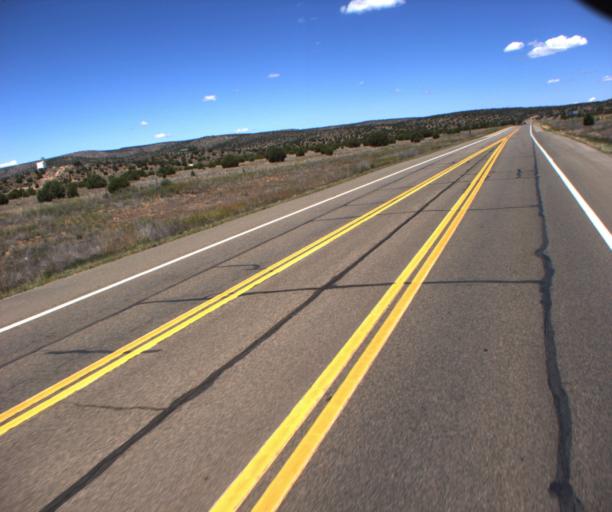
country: US
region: Arizona
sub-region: Yavapai County
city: Paulden
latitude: 34.9119
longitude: -112.4593
